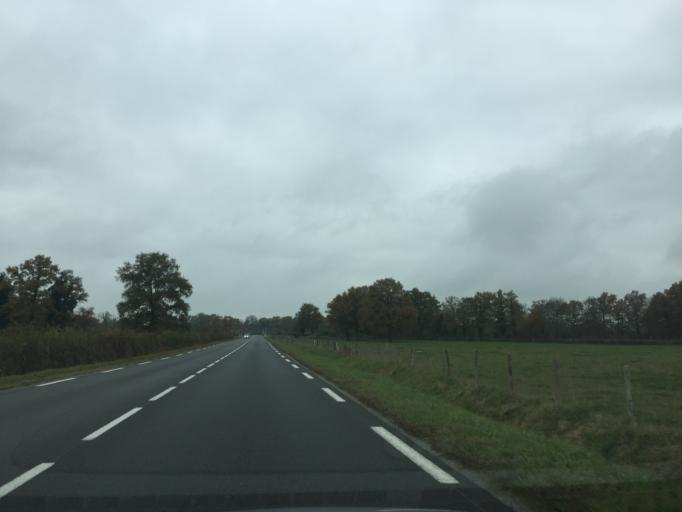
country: FR
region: Limousin
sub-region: Departement de la Creuse
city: Gouzon
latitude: 46.1447
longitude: 2.2028
